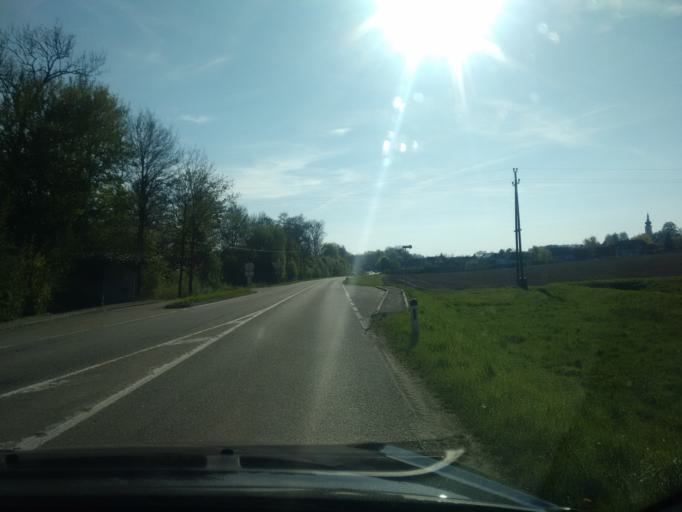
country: AT
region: Upper Austria
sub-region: Wels-Land
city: Buchkirchen
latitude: 48.2229
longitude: 14.0288
